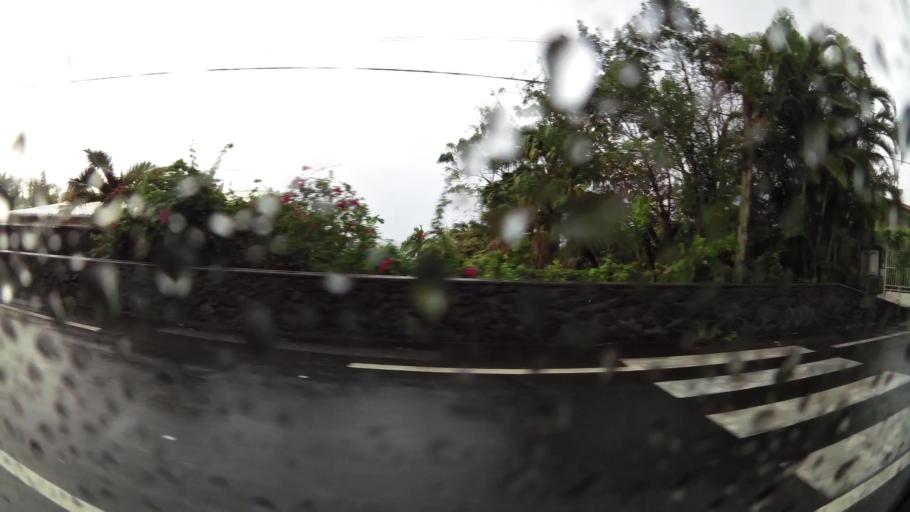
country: RE
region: Reunion
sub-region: Reunion
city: Saint-Benoit
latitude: -21.0294
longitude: 55.7084
